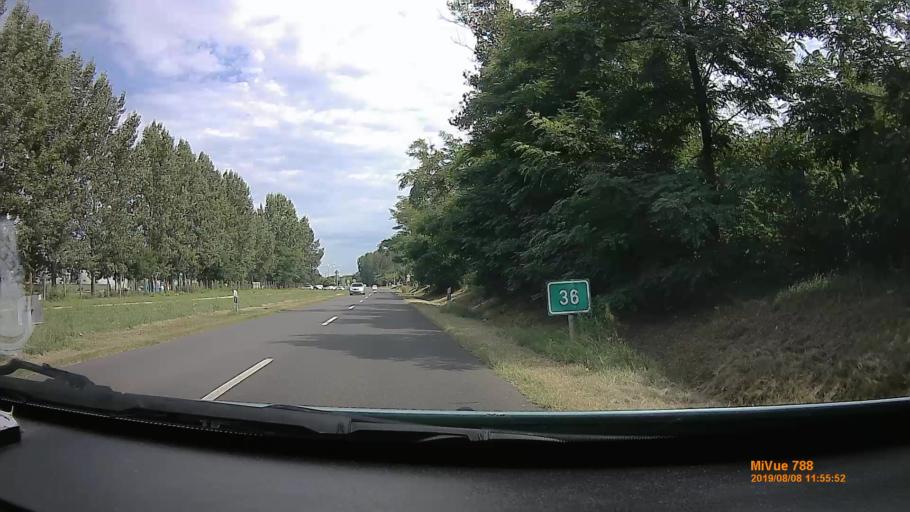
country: HU
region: Szabolcs-Szatmar-Bereg
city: Nyirmihalydi
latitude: 47.7456
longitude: 21.9853
